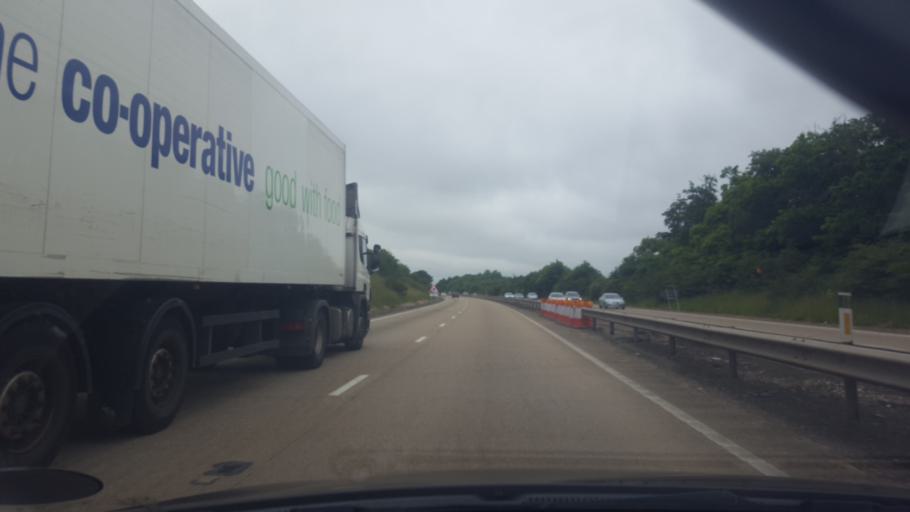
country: GB
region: England
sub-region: Essex
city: Alresford
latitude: 51.8922
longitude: 1.0106
